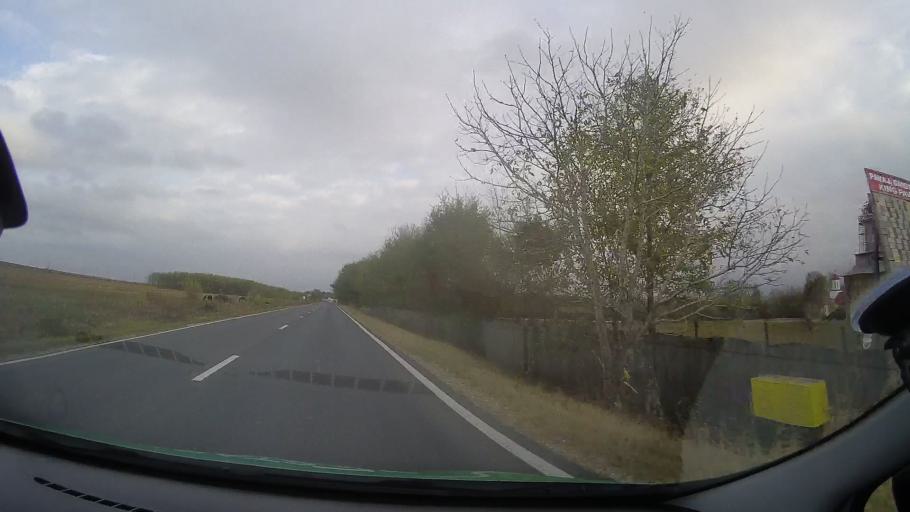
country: RO
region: Constanta
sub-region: Comuna Mircea Voda
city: Satu Nou
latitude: 44.2657
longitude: 28.2496
